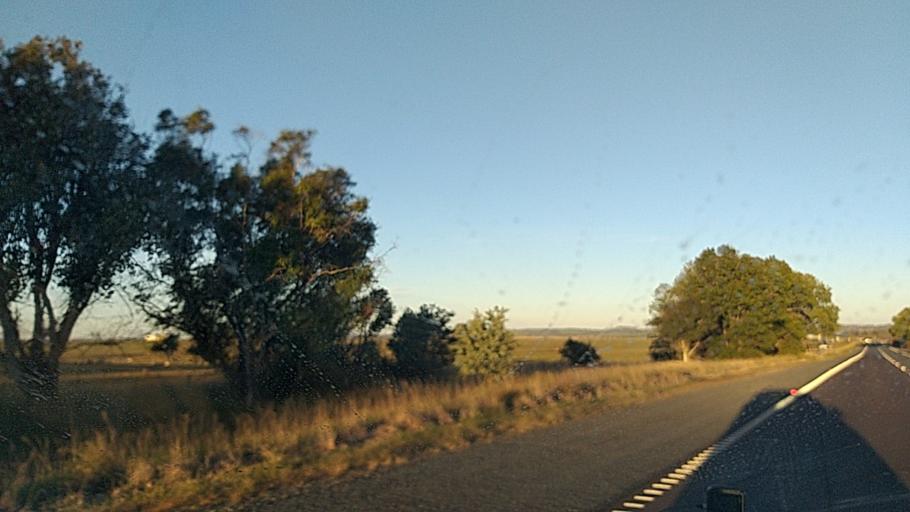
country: AU
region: New South Wales
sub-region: Goulburn Mulwaree
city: Goulburn
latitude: -34.8382
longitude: 149.5754
